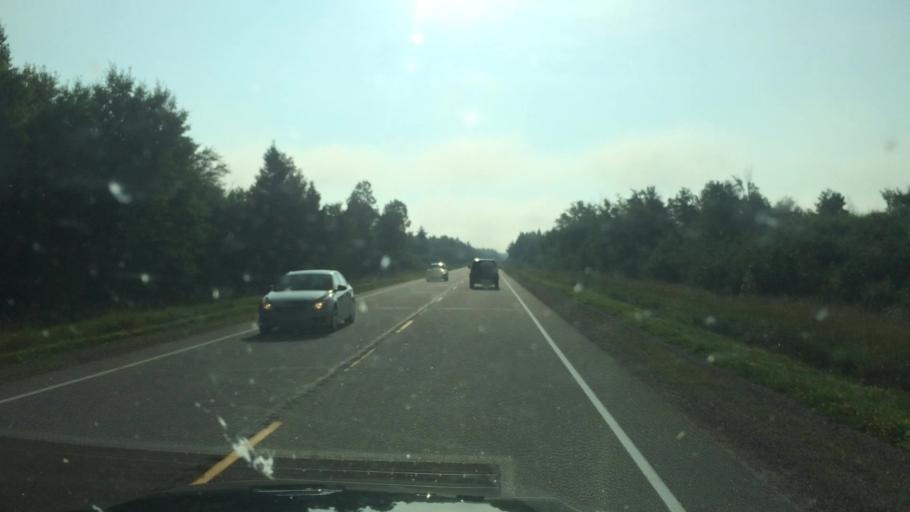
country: US
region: Wisconsin
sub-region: Langlade County
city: Antigo
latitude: 45.1462
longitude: -89.3318
